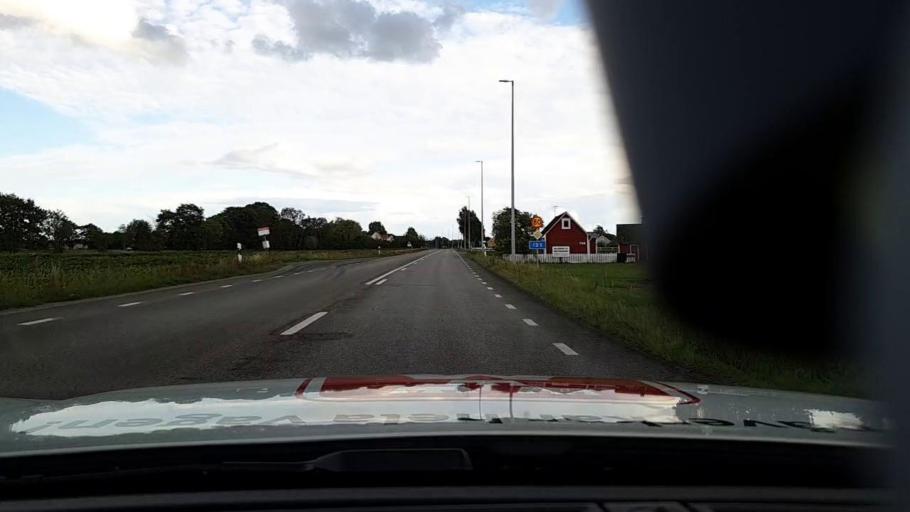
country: SE
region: Blekinge
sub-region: Solvesborgs Kommun
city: Soelvesborg
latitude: 56.0511
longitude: 14.6513
